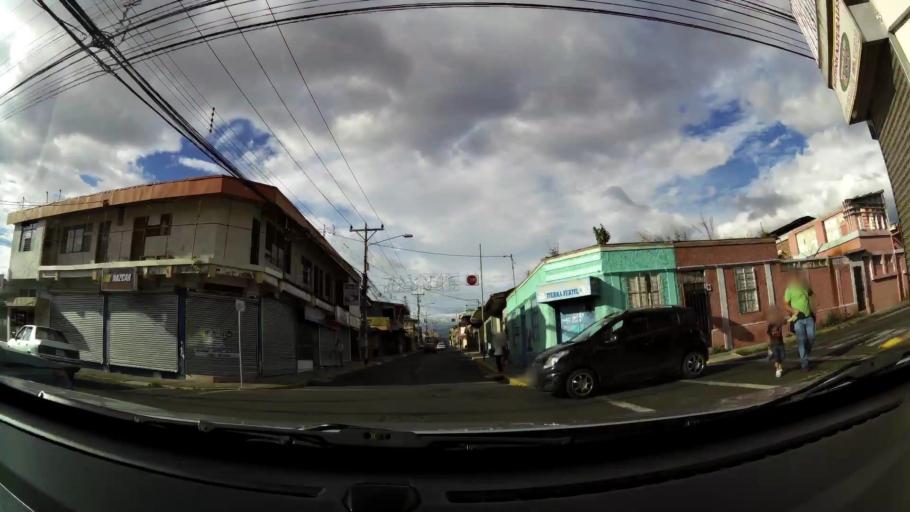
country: CR
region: Alajuela
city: Alajuela
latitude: 10.0126
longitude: -84.2132
